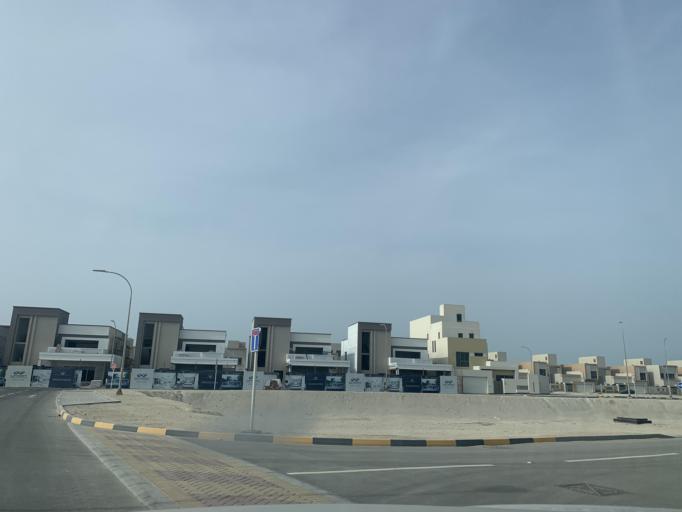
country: BH
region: Muharraq
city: Al Muharraq
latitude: 26.3222
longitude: 50.6281
